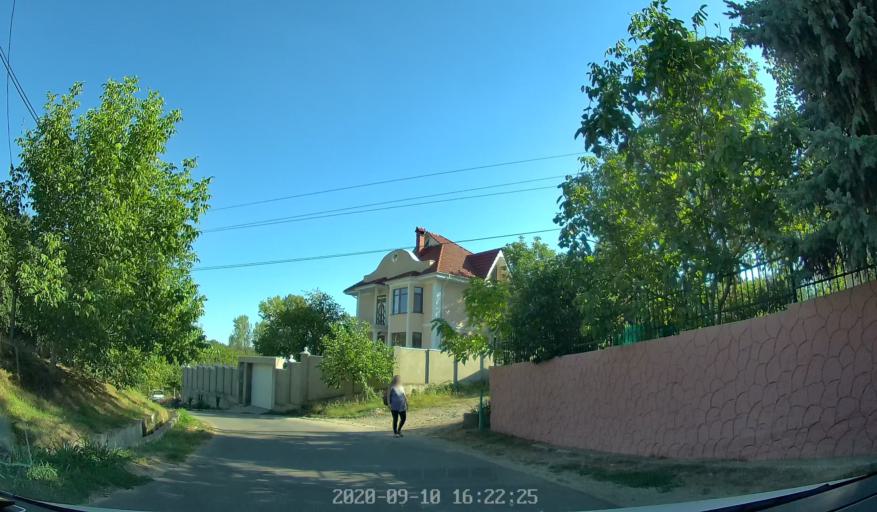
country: MD
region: Chisinau
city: Stauceni
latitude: 47.0530
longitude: 28.9247
